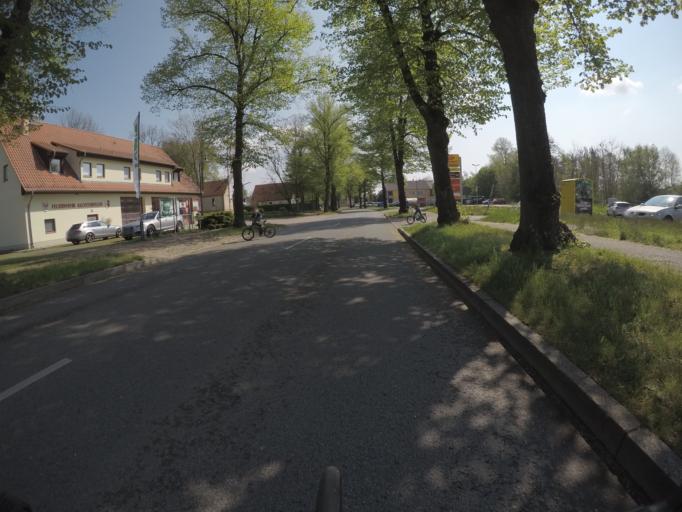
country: DE
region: Brandenburg
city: Wandlitz
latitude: 52.7910
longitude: 13.4811
